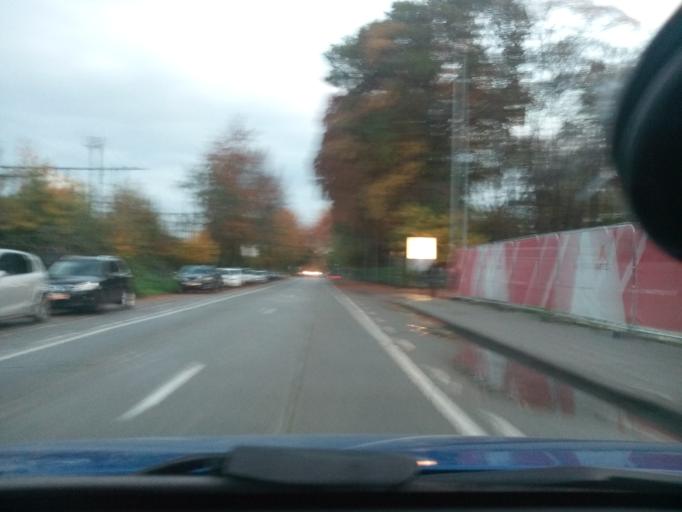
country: BE
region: Flanders
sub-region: Provincie West-Vlaanderen
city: Brugge
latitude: 51.1939
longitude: 3.2186
